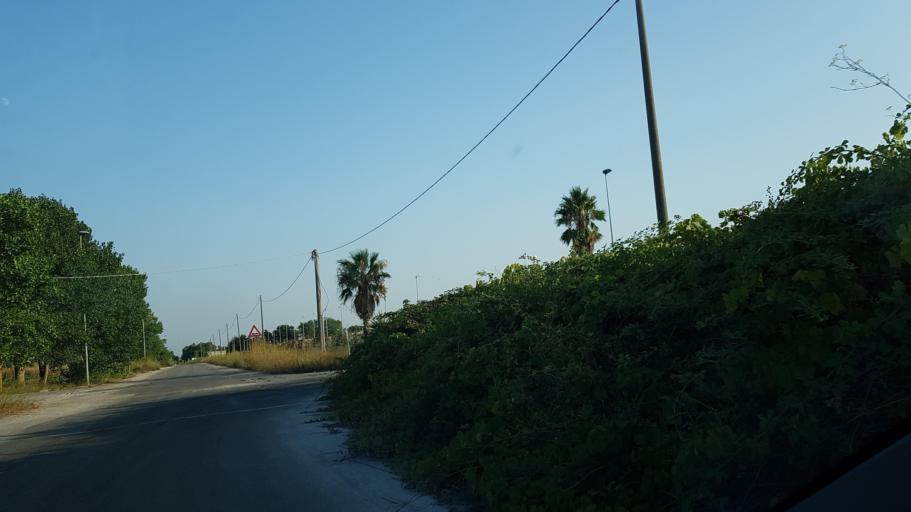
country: IT
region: Apulia
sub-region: Provincia di Brindisi
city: Materdomini
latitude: 40.6386
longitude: 17.9710
